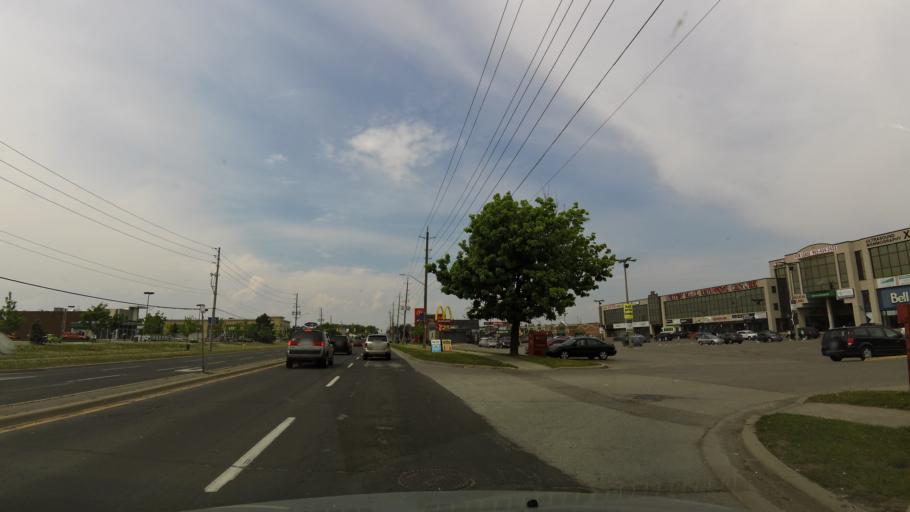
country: CA
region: Ontario
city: Oshawa
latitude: 43.8831
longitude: -78.9113
